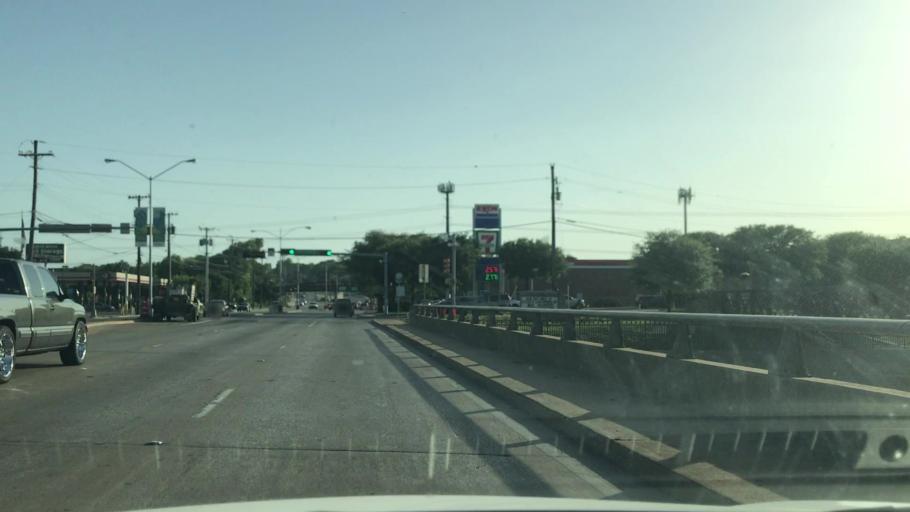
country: US
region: Texas
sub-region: Dallas County
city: Highland Park
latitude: 32.8132
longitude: -96.7264
